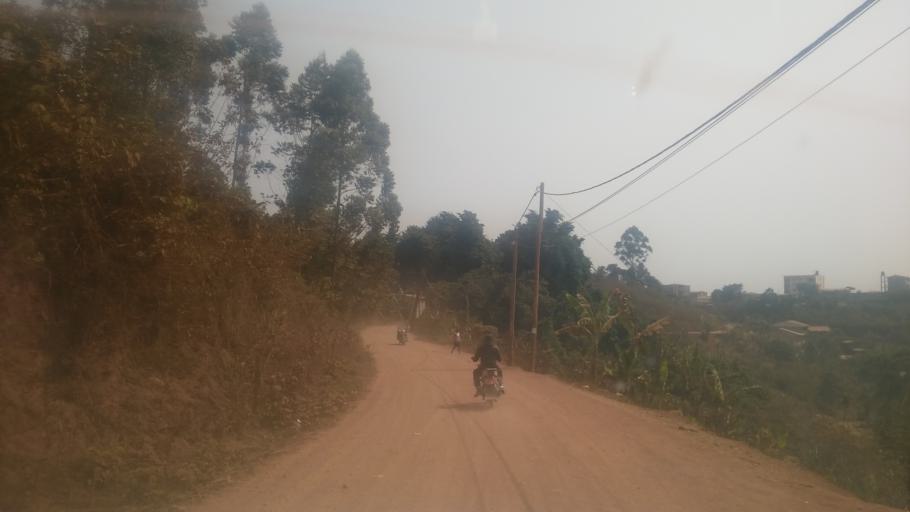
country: CM
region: West
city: Dschang
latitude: 5.4636
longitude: 10.0687
